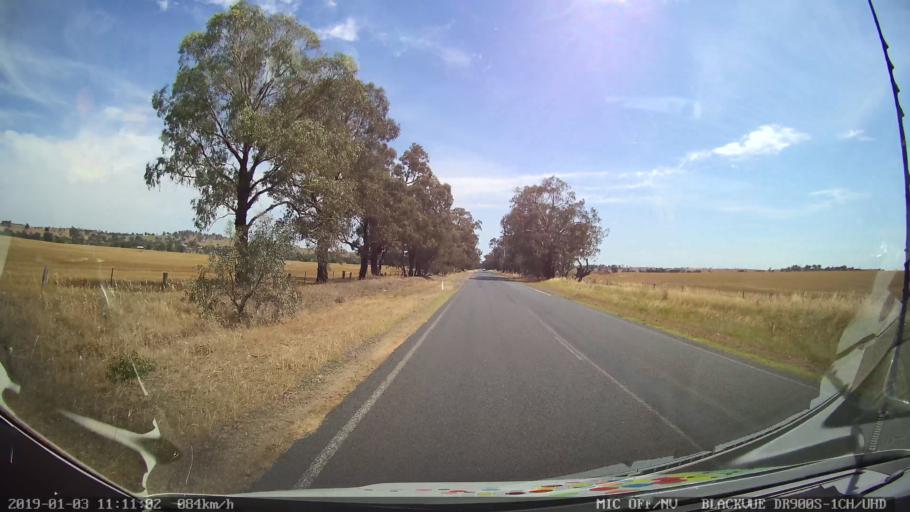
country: AU
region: New South Wales
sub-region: Young
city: Young
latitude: -34.2198
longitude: 148.2591
